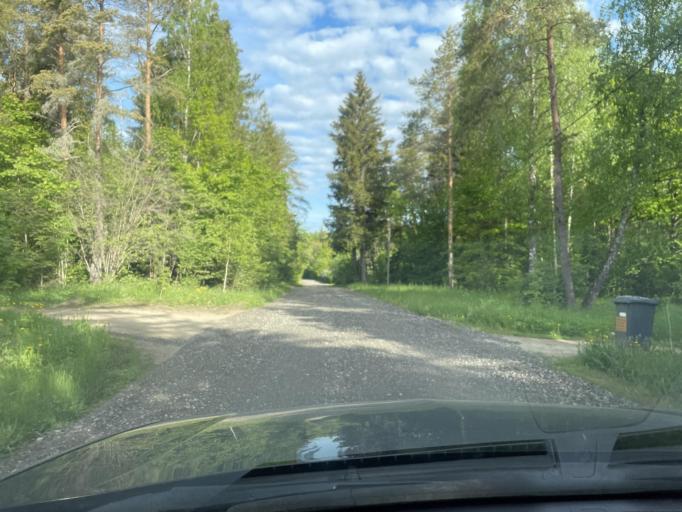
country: EE
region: Harju
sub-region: Keila linn
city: Keila
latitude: 59.3020
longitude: 24.3059
